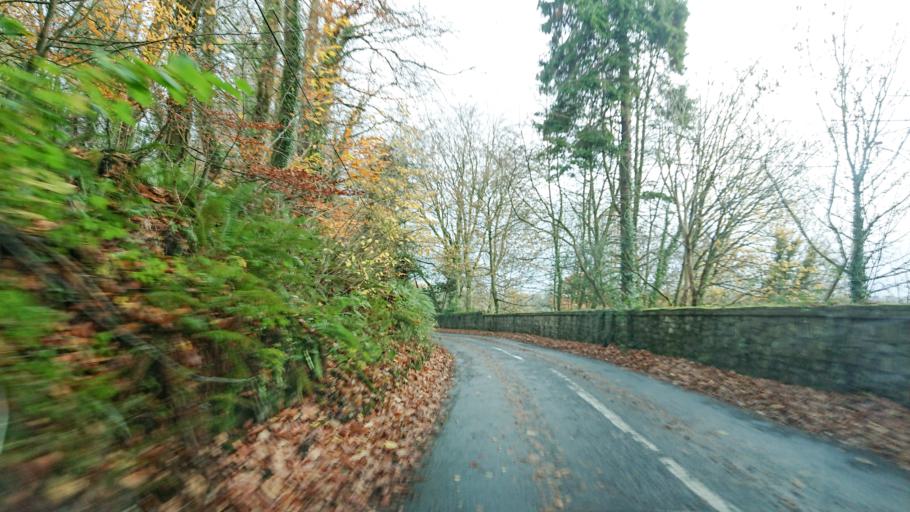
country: IE
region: Munster
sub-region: South Tipperary
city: Cluain Meala
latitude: 52.3573
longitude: -7.5996
